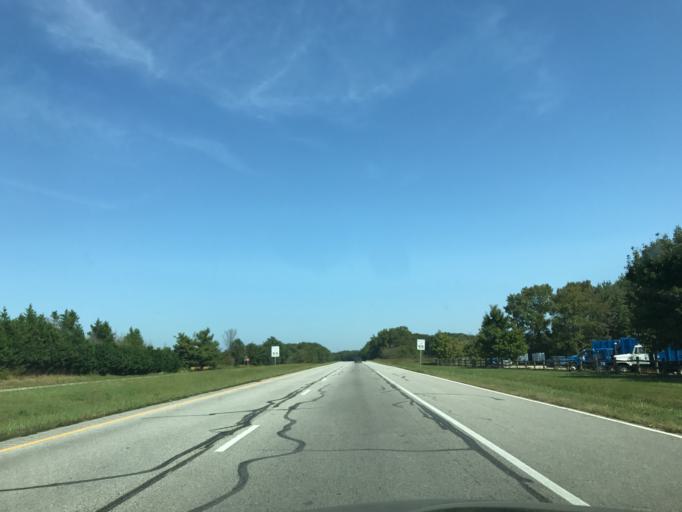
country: US
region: Maryland
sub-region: Queen Anne's County
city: Kingstown
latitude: 39.2743
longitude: -75.8613
